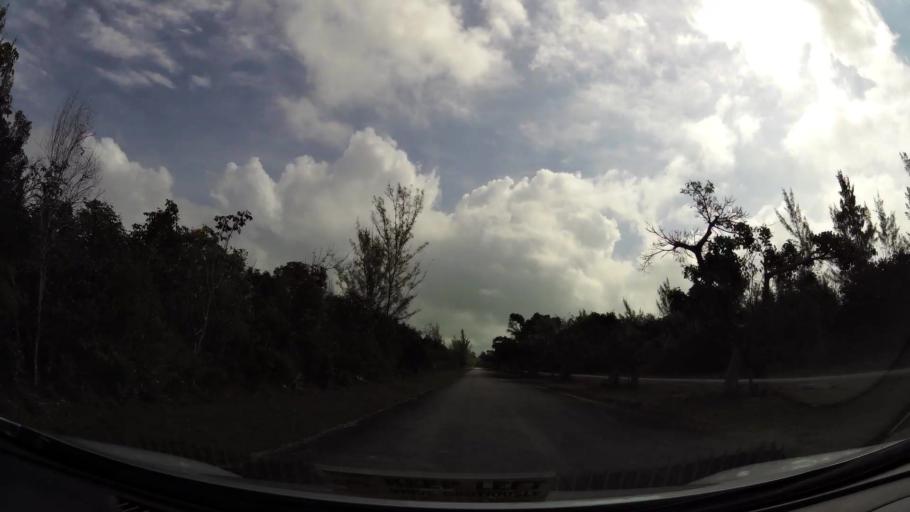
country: BS
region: Freeport
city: Lucaya
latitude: 26.5516
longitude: -78.5516
